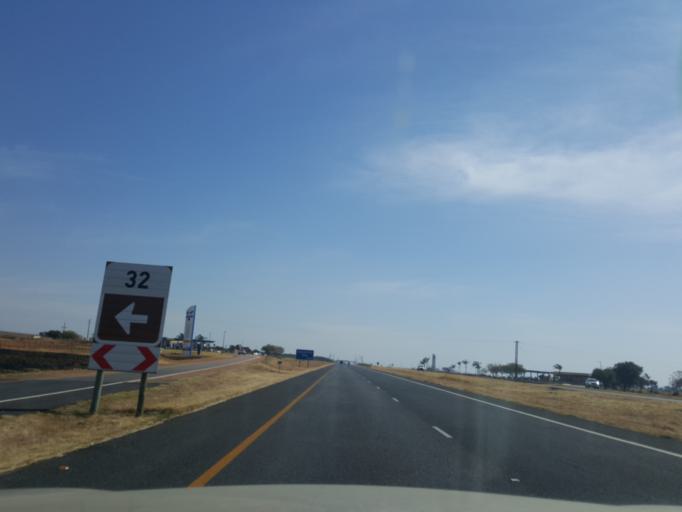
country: ZA
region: Gauteng
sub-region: City of Tshwane Metropolitan Municipality
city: Cullinan
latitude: -25.7986
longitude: 28.5724
